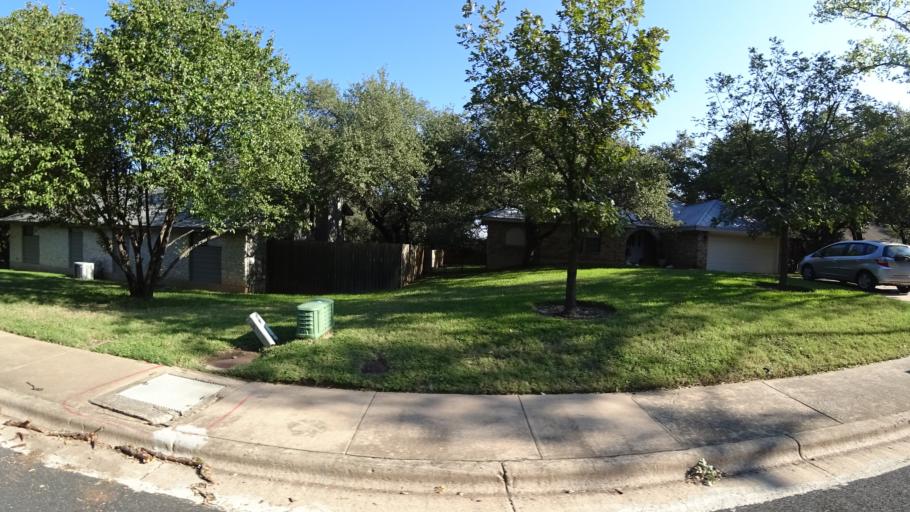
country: US
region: Texas
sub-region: Travis County
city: Rollingwood
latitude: 30.2702
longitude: -97.7972
